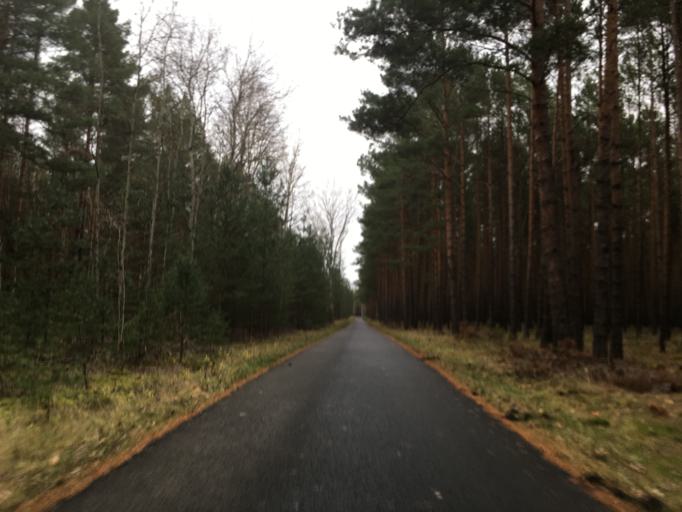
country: DE
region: Brandenburg
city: Mullrose
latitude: 52.2275
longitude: 14.4451
